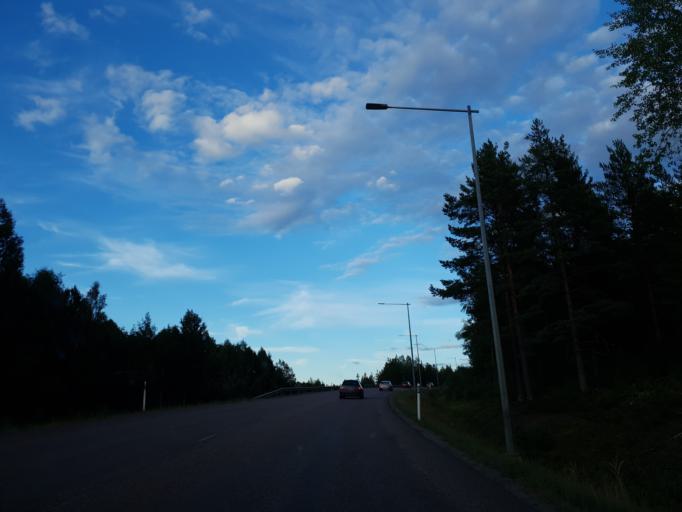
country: SE
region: Gaevleborg
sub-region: Soderhamns Kommun
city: Soderhamn
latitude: 61.2921
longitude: 17.0534
